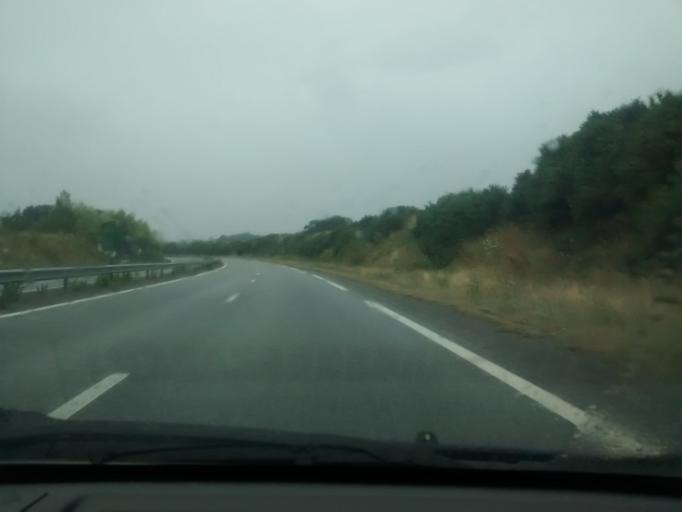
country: FR
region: Brittany
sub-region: Departement d'Ille-et-Vilaine
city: Cesson-Sevigne
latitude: 48.1445
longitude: -1.6255
